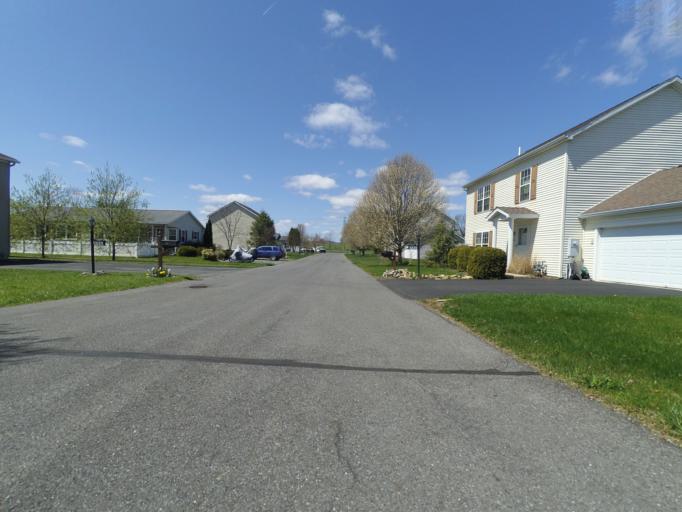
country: US
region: Pennsylvania
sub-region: Centre County
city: Houserville
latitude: 40.8355
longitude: -77.8089
